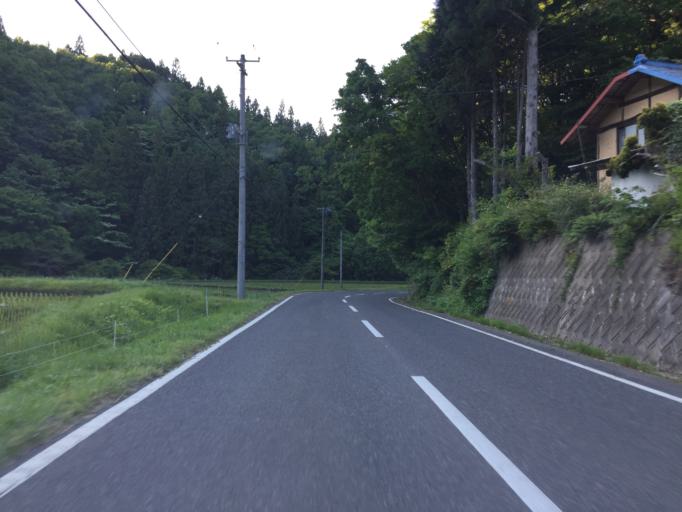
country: JP
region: Ibaraki
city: Daigo
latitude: 36.9232
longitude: 140.4892
